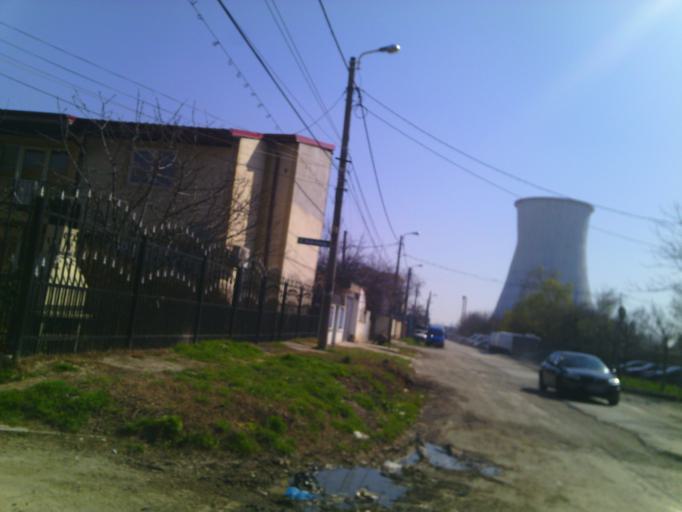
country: RO
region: Ilfov
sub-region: Comuna Jilava
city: Jilava
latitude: 44.3760
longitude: 26.1031
